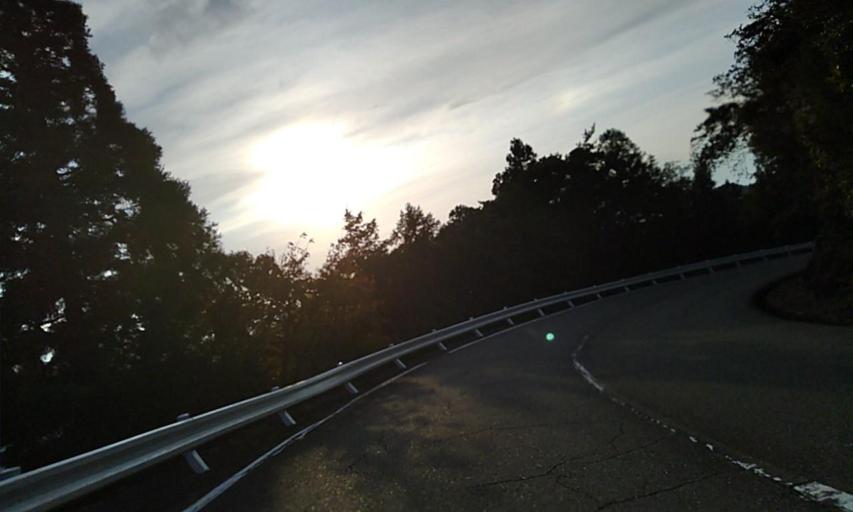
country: JP
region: Mie
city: Ise
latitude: 34.4591
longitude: 136.7706
